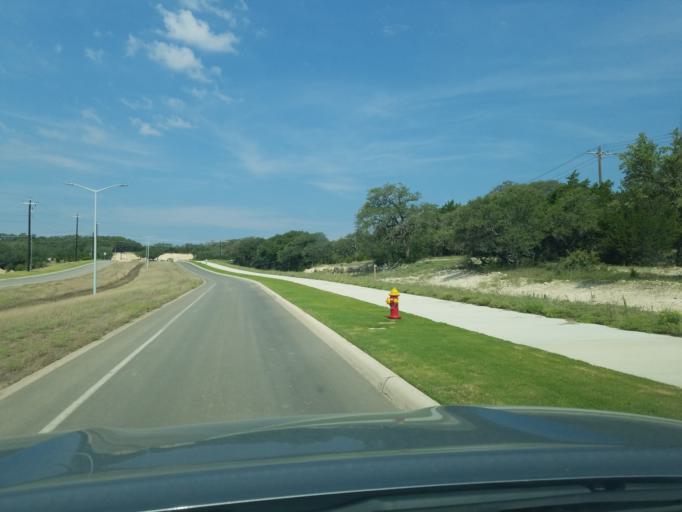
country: US
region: Texas
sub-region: Kendall County
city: Boerne
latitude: 29.7565
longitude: -98.7165
